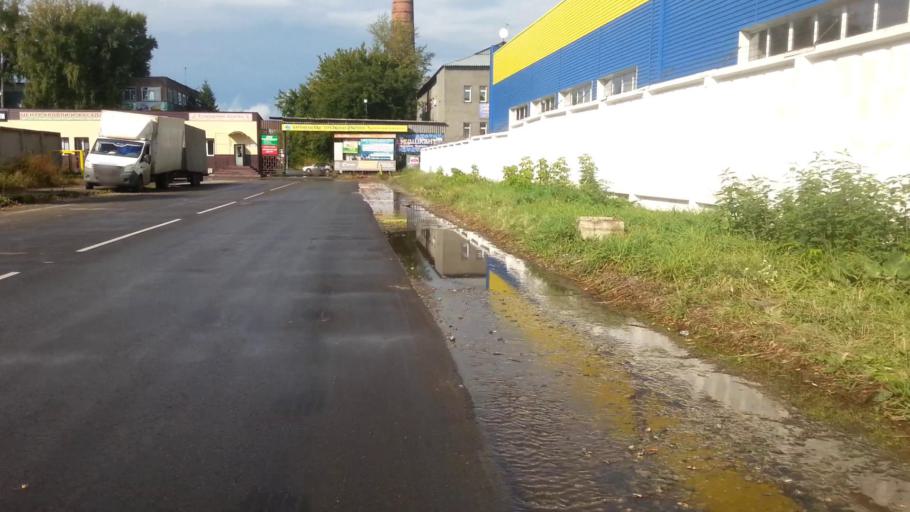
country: RU
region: Altai Krai
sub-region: Gorod Barnaulskiy
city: Barnaul
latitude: 53.3438
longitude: 83.7231
